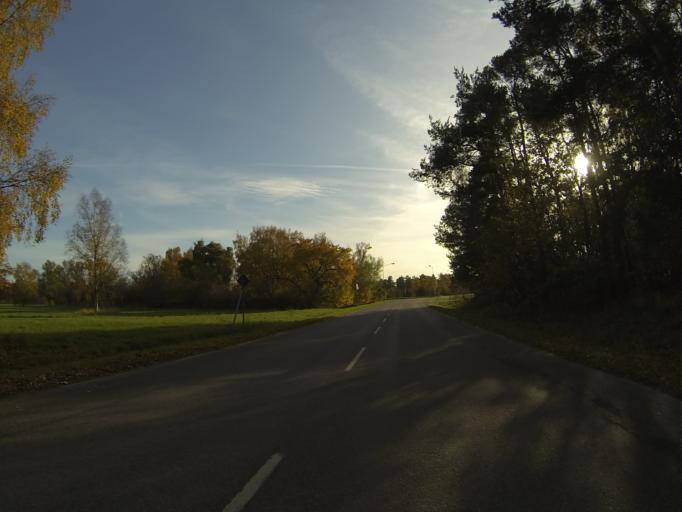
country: SE
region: Skane
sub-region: Hoors Kommun
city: Loberod
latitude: 55.7246
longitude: 13.4653
